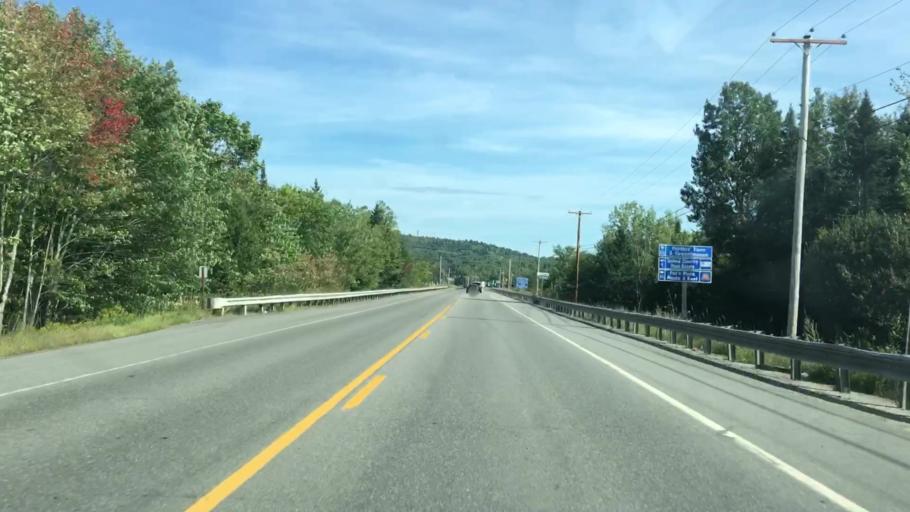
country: US
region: Maine
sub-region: Penobscot County
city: Lincoln
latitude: 45.3563
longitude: -68.5388
